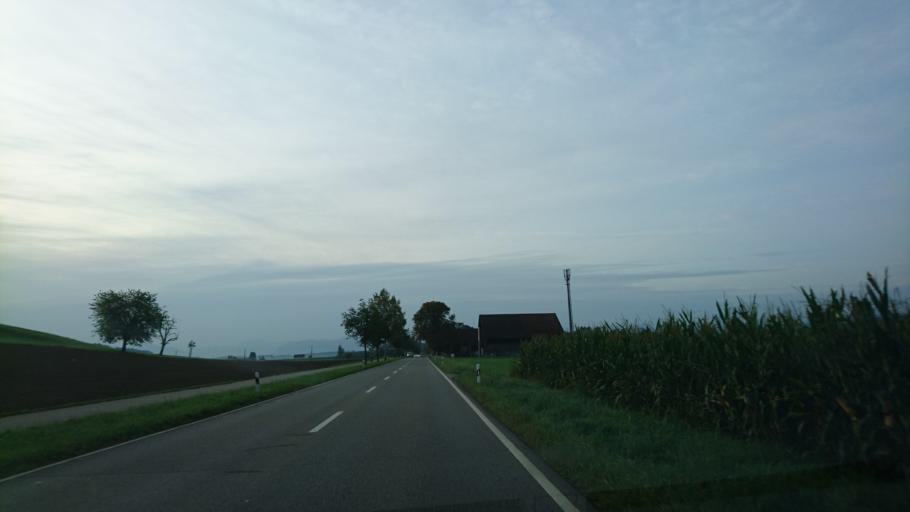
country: CH
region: Zurich
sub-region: Bezirk Uster
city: Monchaltorf
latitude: 47.3208
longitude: 8.7158
